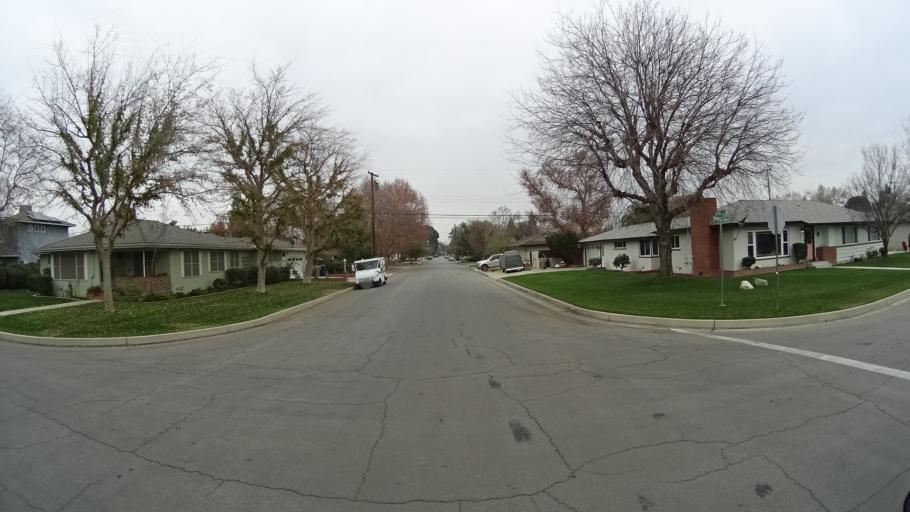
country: US
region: California
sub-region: Kern County
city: Bakersfield
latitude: 35.3847
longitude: -119.0314
